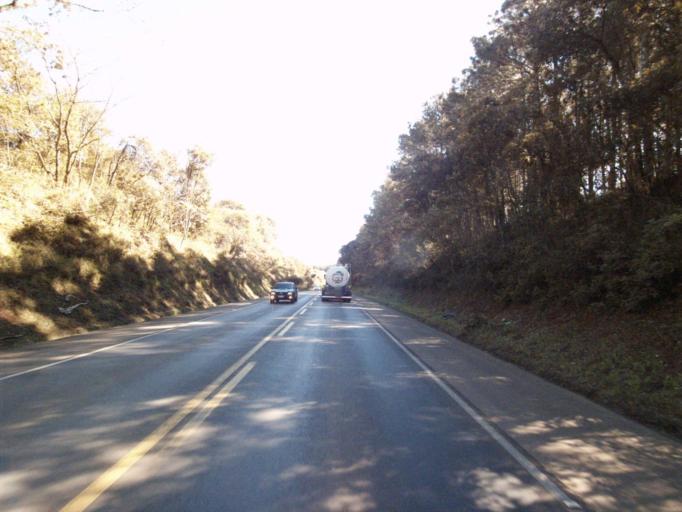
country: BR
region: Santa Catarina
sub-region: Xanxere
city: Xanxere
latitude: -26.8706
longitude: -52.3059
